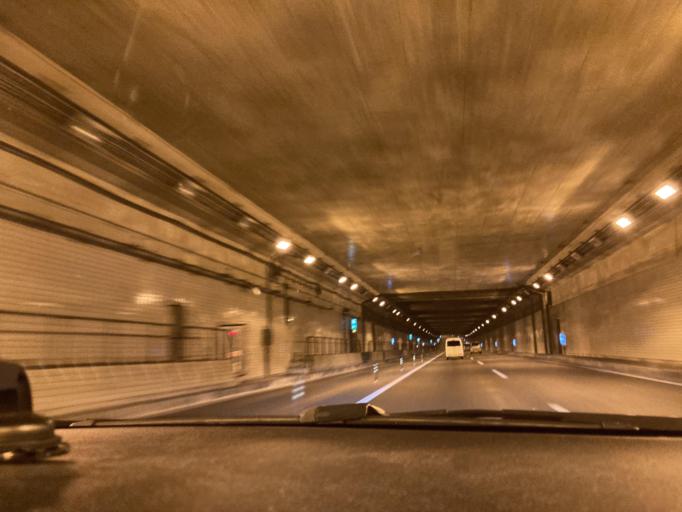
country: JP
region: Okinawa
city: Naha-shi
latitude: 26.2136
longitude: 127.6559
